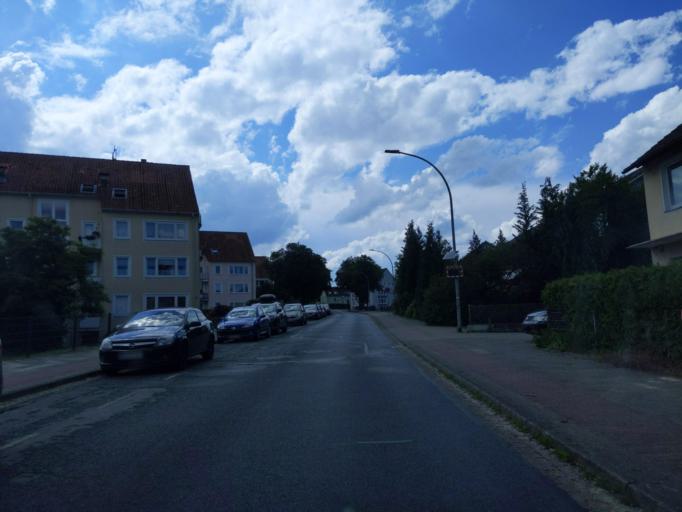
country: DE
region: Lower Saxony
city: Walsrode
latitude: 52.8674
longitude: 9.5895
